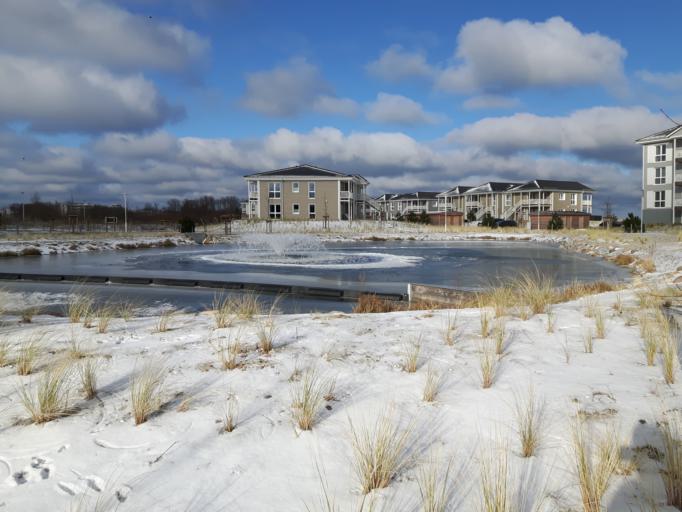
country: DE
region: Schleswig-Holstein
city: Heiligenhafen
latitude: 54.3794
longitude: 10.9780
